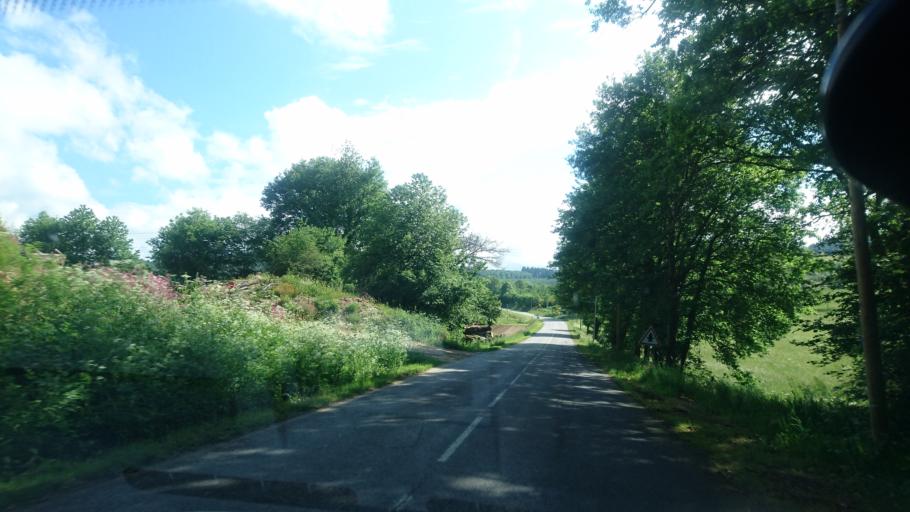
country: FR
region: Limousin
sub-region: Departement de la Haute-Vienne
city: Peyrat-le-Chateau
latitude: 45.8102
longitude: 1.7963
